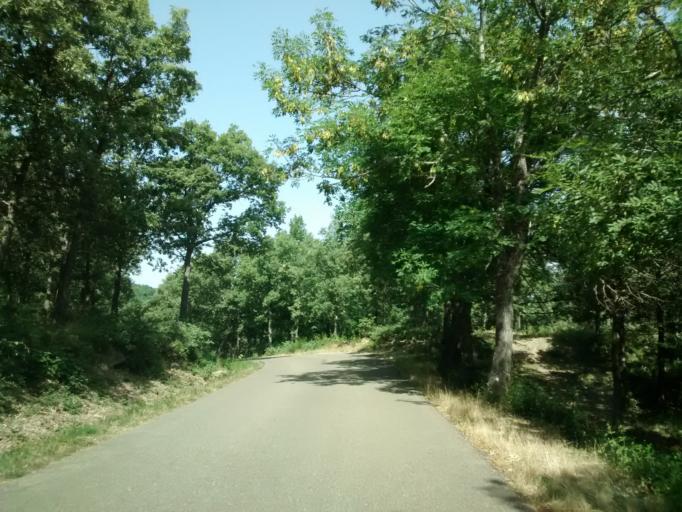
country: ES
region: Castille and Leon
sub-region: Provincia de Soria
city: Vozmediano
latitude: 41.8143
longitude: -1.8186
